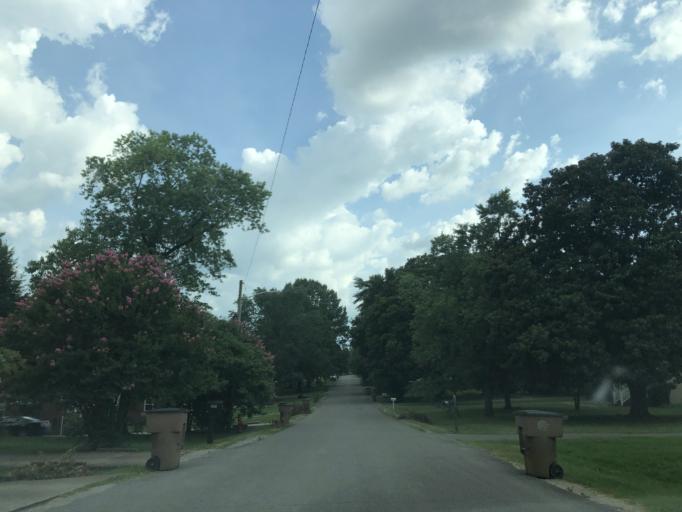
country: US
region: Tennessee
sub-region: Davidson County
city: Lakewood
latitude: 36.1669
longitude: -86.6787
